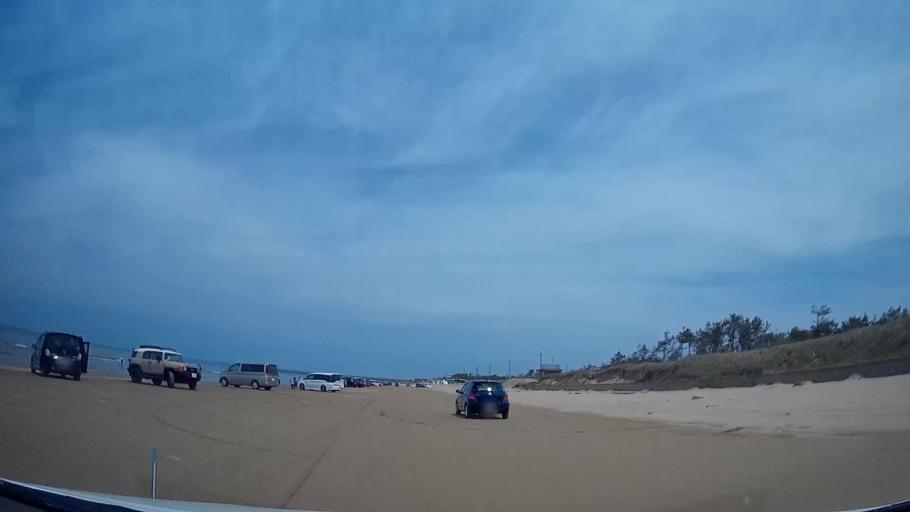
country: JP
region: Ishikawa
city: Hakui
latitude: 36.8394
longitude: 136.7491
